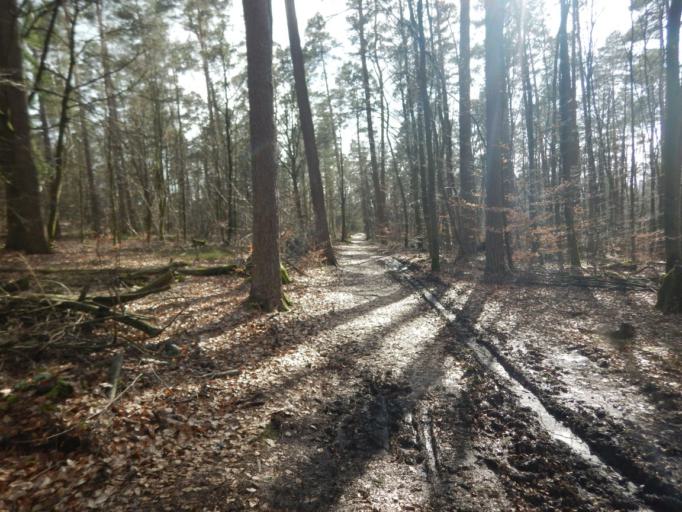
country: LU
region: Grevenmacher
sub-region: Canton d'Echternach
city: Beaufort
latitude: 49.8254
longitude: 6.3205
